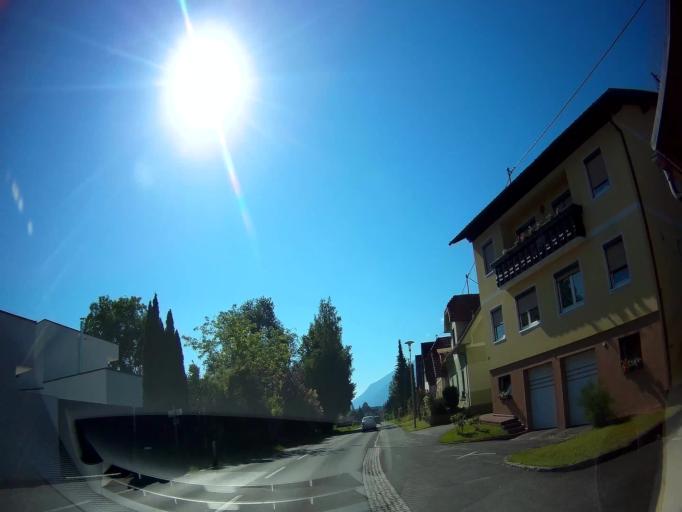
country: AT
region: Carinthia
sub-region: Politischer Bezirk Volkermarkt
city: Eberndorf
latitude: 46.5903
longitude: 14.6422
